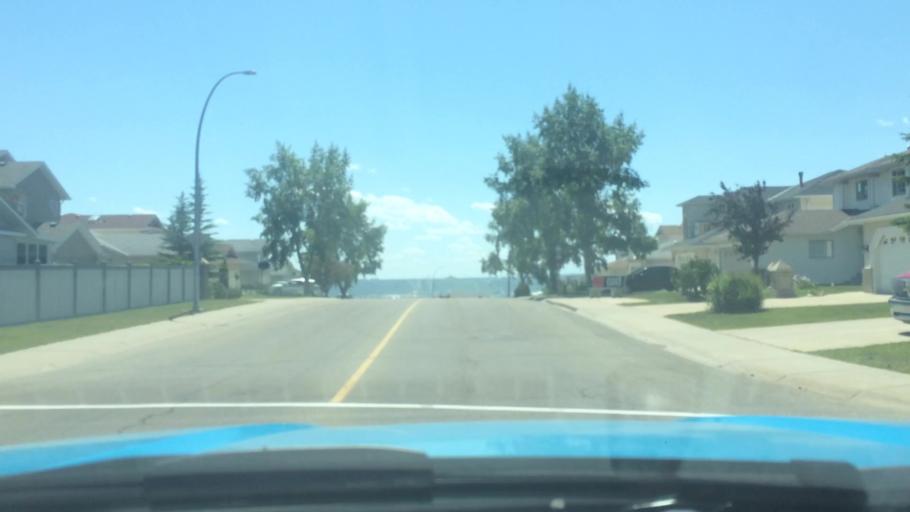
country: CA
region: Alberta
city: Calgary
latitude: 51.1353
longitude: -114.1918
